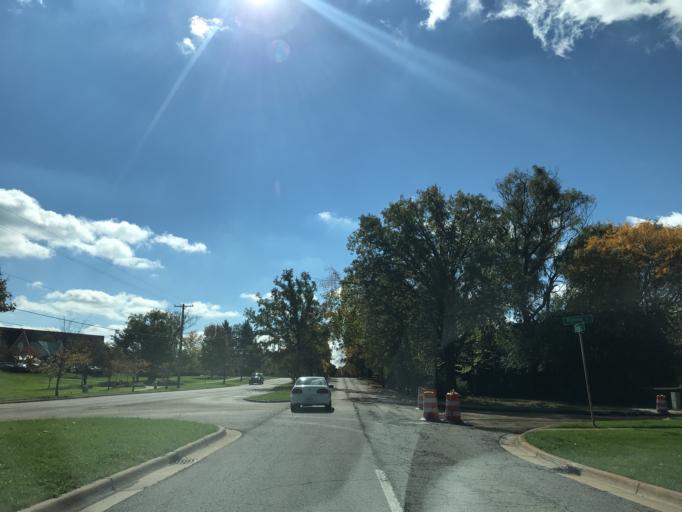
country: US
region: Michigan
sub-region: Washtenaw County
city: Ann Arbor
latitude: 42.2922
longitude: -83.6825
